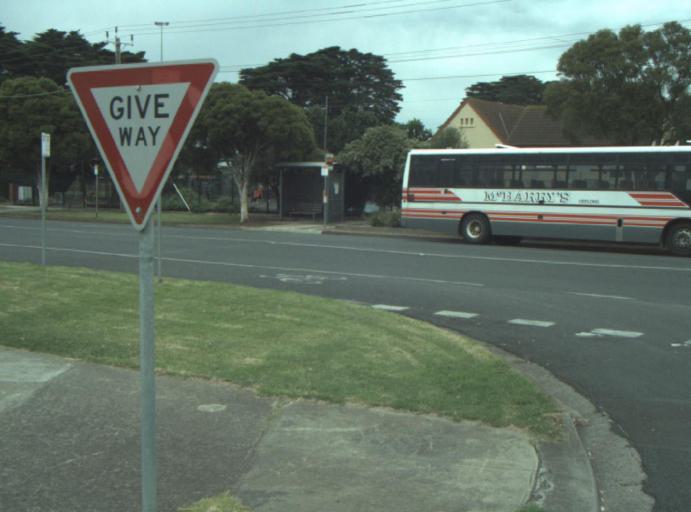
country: AU
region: Victoria
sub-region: Greater Geelong
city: Breakwater
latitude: -38.1754
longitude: 144.3835
